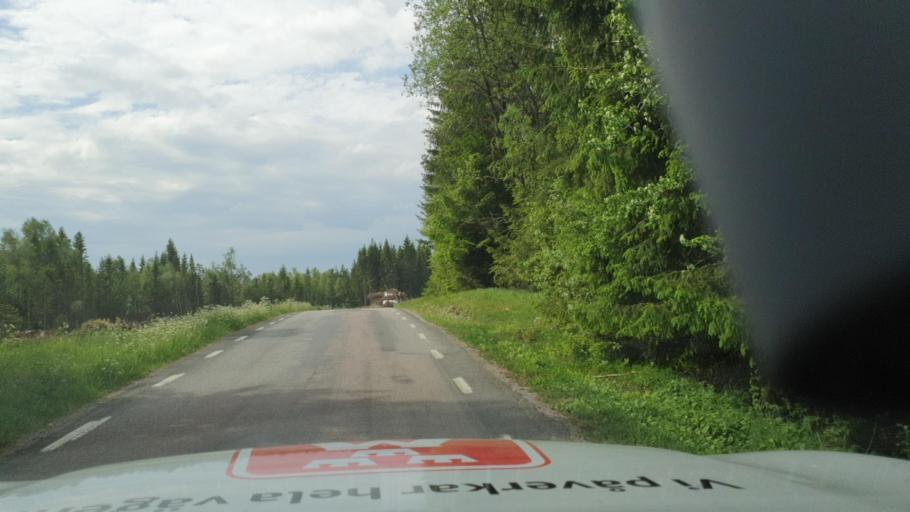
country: SE
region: Vaestra Goetaland
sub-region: Falkopings Kommun
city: Floby
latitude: 57.9834
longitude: 13.4003
